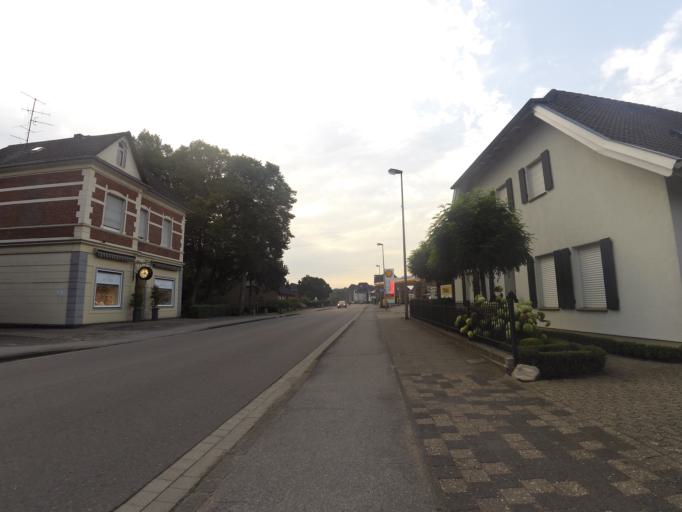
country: DE
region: North Rhine-Westphalia
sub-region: Regierungsbezirk Munster
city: Isselburg
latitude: 51.8480
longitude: 6.4236
